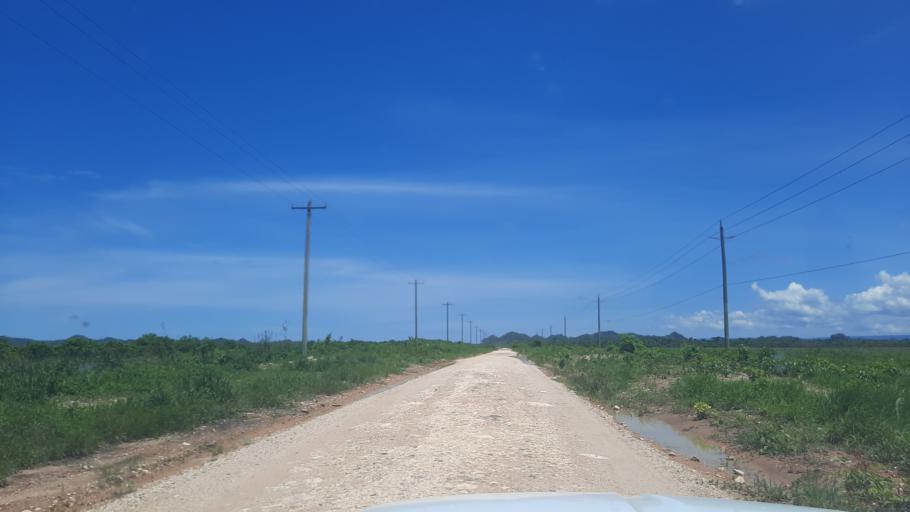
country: BZ
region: Cayo
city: Belmopan
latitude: 17.3365
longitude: -88.5105
